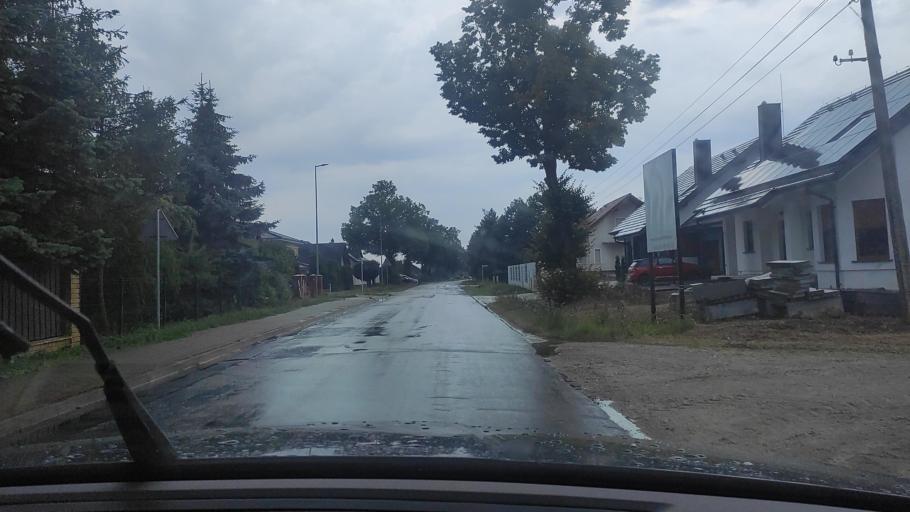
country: PL
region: Greater Poland Voivodeship
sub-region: Powiat poznanski
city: Kleszczewo
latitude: 52.2956
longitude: 17.1509
